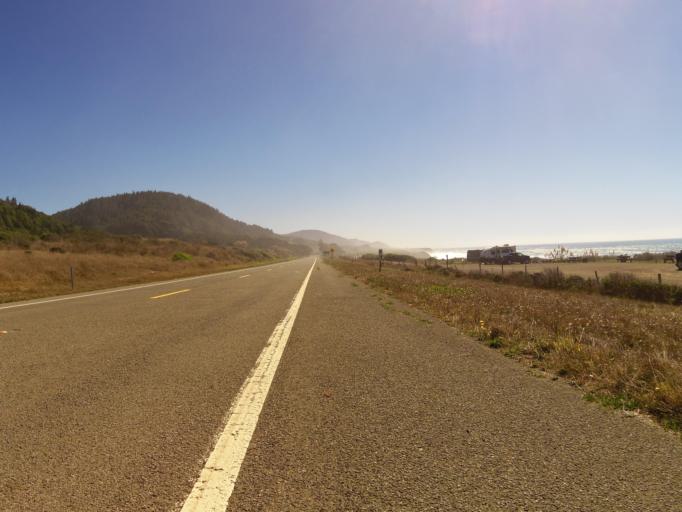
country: US
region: California
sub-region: Mendocino County
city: Fort Bragg
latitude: 39.6840
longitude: -123.7915
